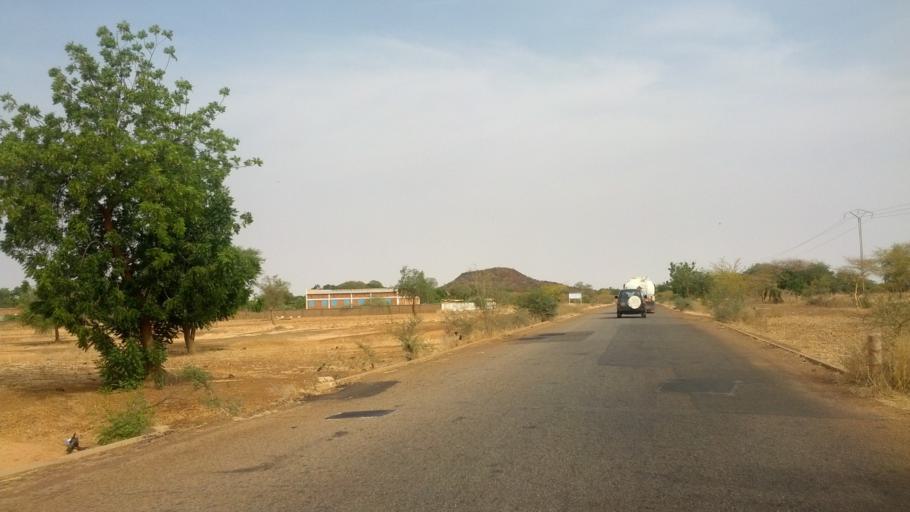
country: BF
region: Centre-Nord
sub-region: Province du Sanmatenga
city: Kaya
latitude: 12.9176
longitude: -1.0779
